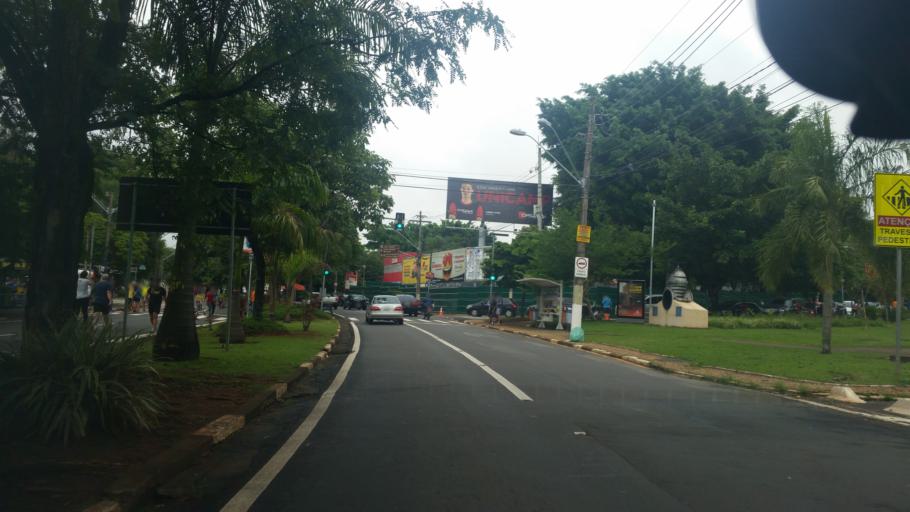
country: BR
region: Sao Paulo
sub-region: Campinas
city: Campinas
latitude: -22.8721
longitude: -47.0481
